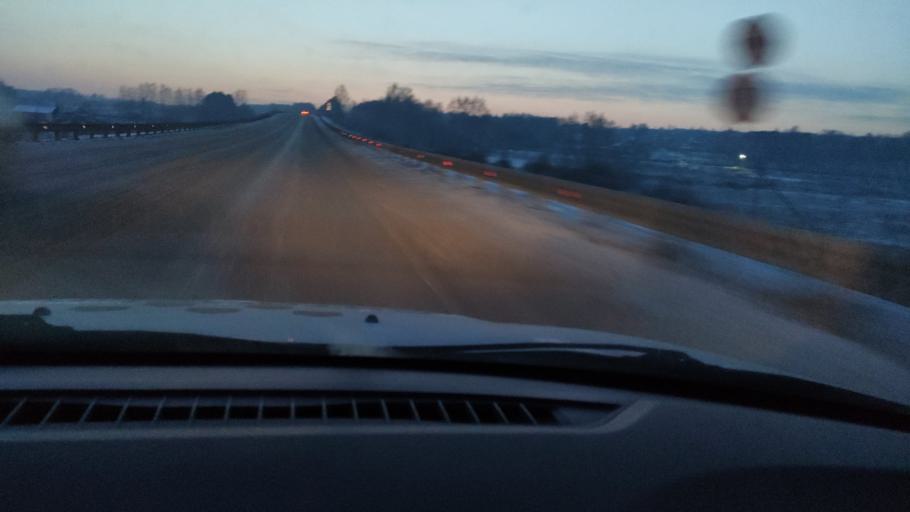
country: RU
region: Perm
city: Kungur
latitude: 57.4237
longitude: 56.9280
